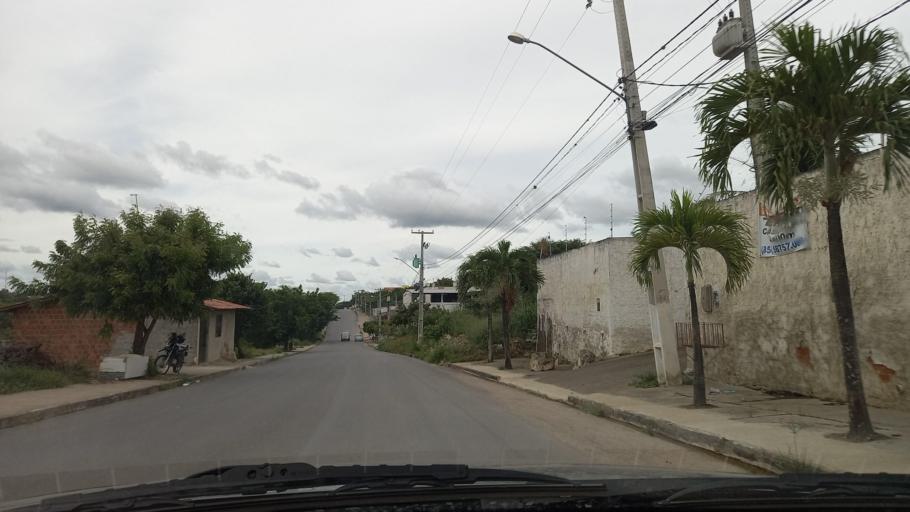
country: BR
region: Pernambuco
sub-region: Gravata
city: Gravata
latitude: -8.2131
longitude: -35.6028
